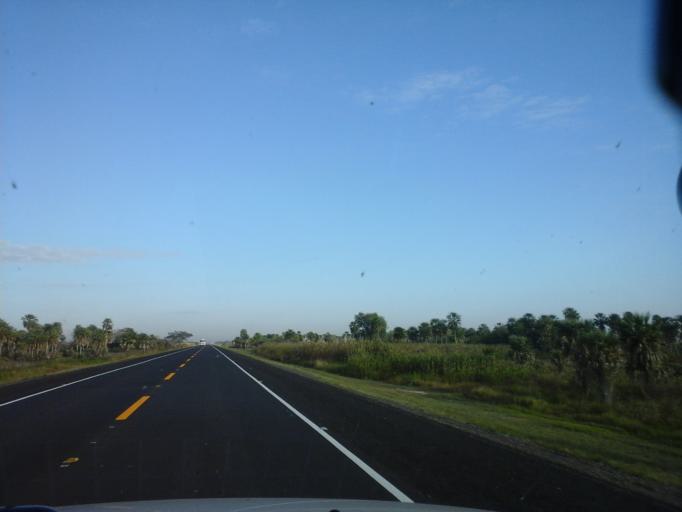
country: PY
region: Neembucu
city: Pilar
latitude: -26.8655
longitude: -57.8268
